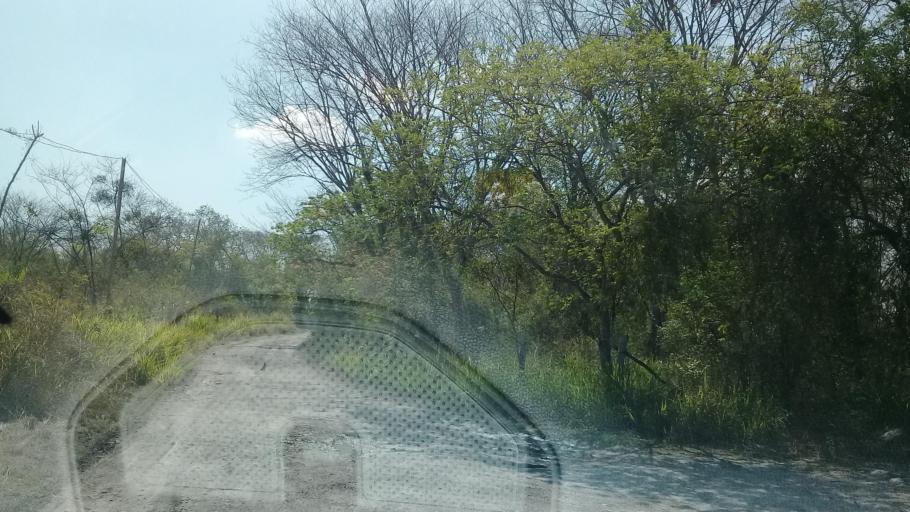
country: MX
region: Veracruz
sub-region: Emiliano Zapata
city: Plan del Rio
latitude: 19.3984
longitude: -96.6196
